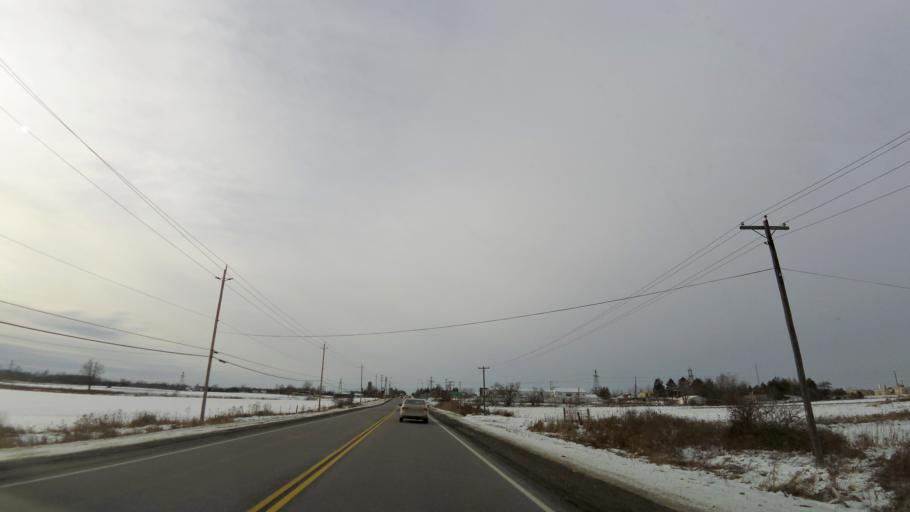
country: CA
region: Ontario
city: Ancaster
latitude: 43.3021
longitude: -79.9441
